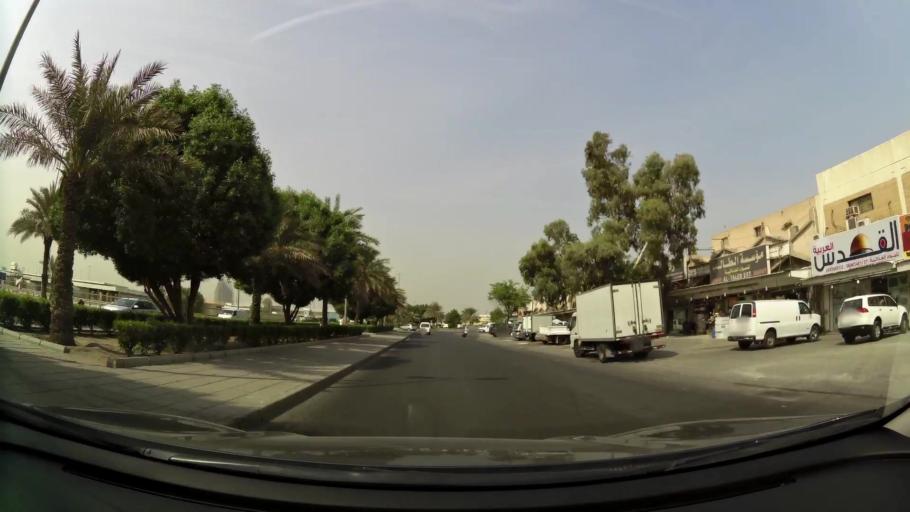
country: KW
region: Al Asimah
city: Ar Rabiyah
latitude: 29.3247
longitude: 47.9288
